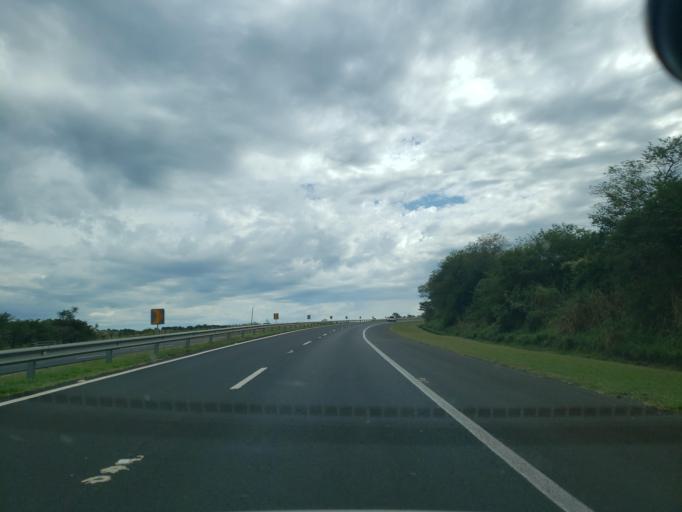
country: BR
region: Sao Paulo
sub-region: Bauru
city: Bauru
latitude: -22.1962
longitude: -49.1964
